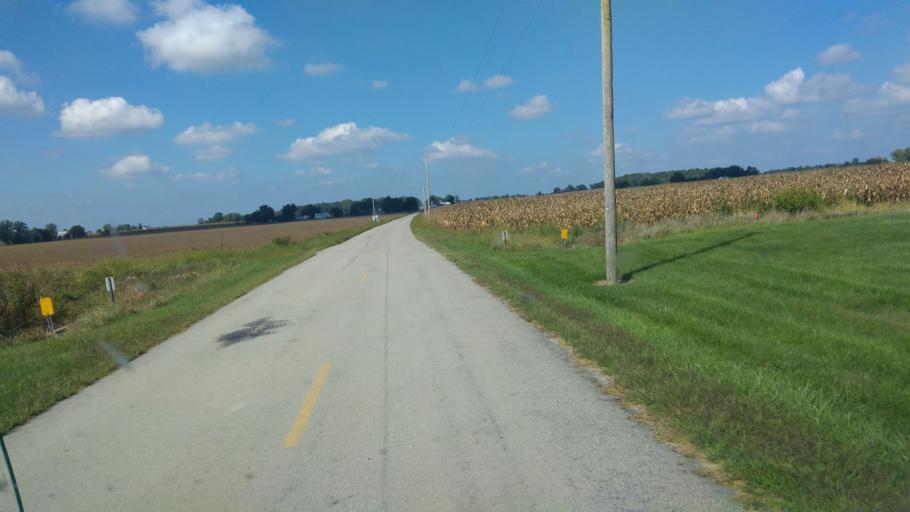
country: US
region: Ohio
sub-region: Logan County
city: Lakeview
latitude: 40.5937
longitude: -83.8802
